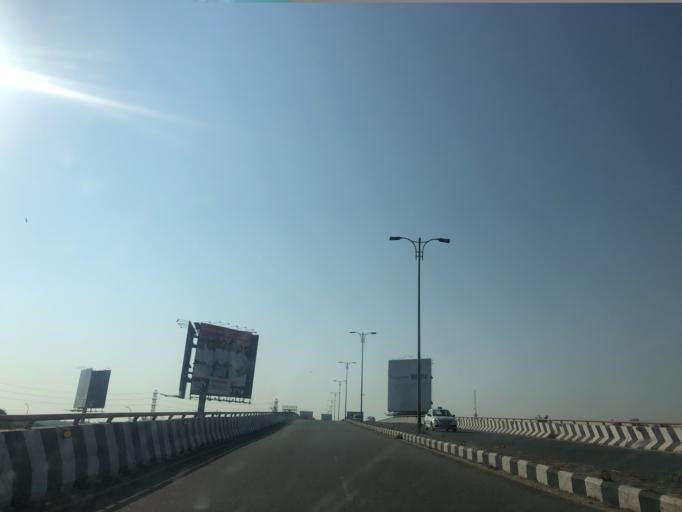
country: IN
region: Telangana
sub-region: Rangareddi
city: Sriramnagar
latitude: 17.2572
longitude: 78.3809
